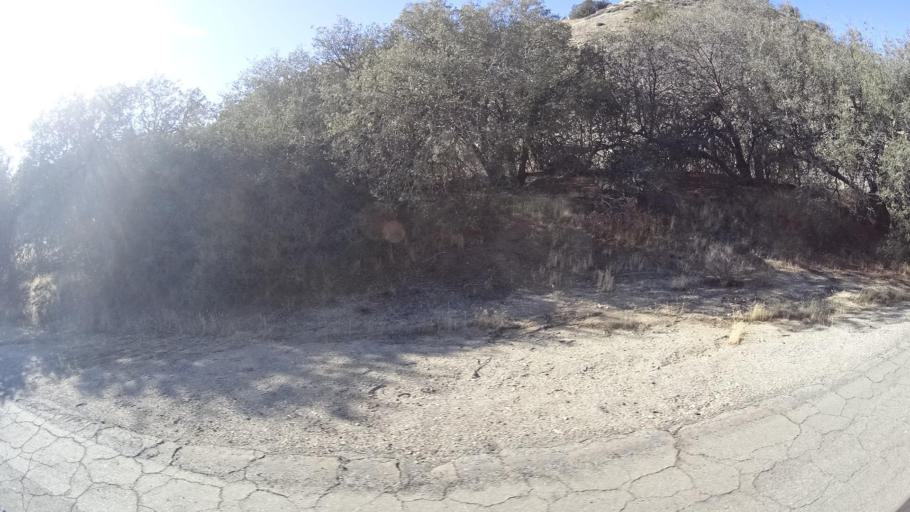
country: US
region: California
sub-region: Kern County
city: Maricopa
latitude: 34.9464
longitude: -119.4012
